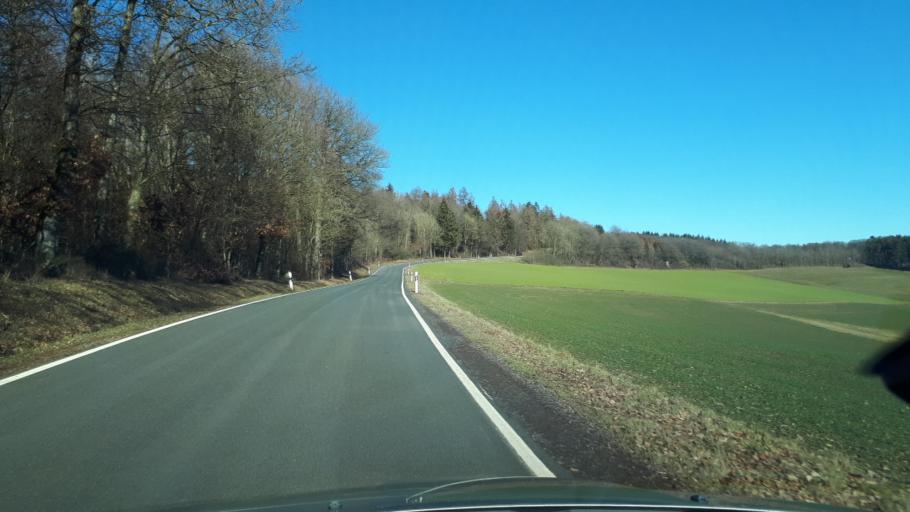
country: DE
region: Rheinland-Pfalz
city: Ellscheid
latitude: 50.1648
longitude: 6.9138
